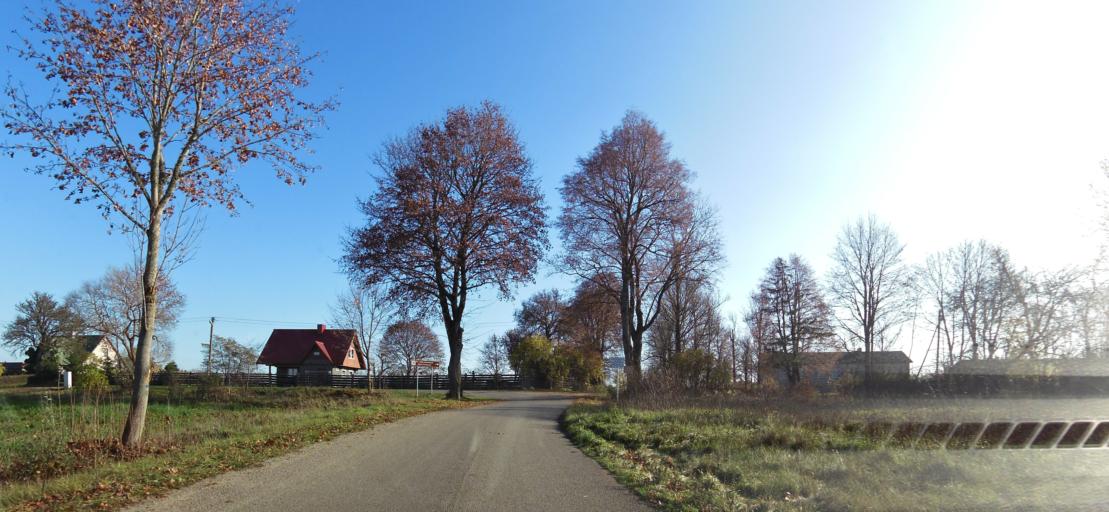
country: LT
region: Vilnius County
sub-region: Vilniaus Rajonas
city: Vievis
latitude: 54.6470
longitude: 24.7425
